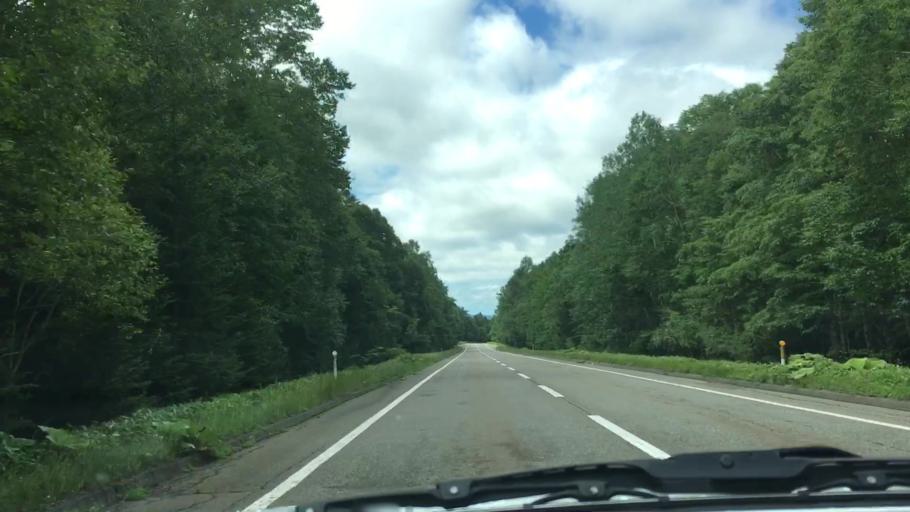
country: JP
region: Hokkaido
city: Kitami
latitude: 43.4123
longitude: 143.9689
